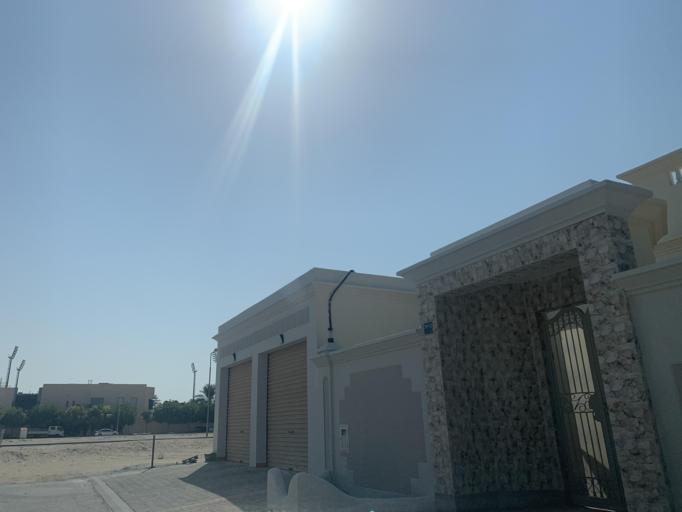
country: BH
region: Central Governorate
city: Madinat Hamad
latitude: 26.1356
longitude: 50.4945
